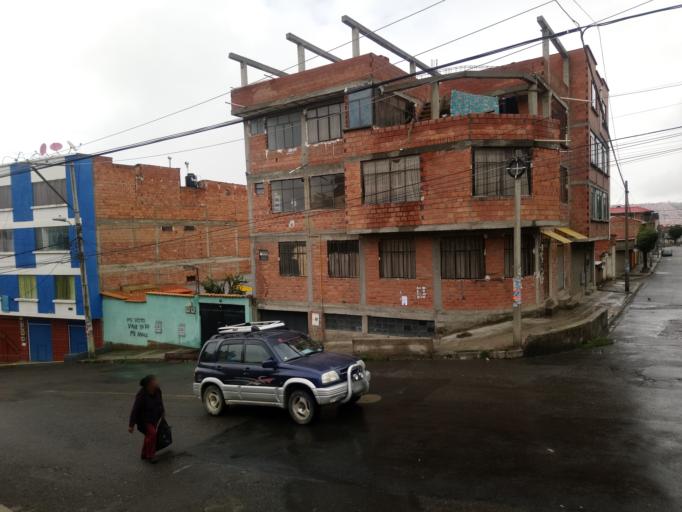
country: BO
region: La Paz
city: La Paz
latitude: -16.4970
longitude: -68.1017
